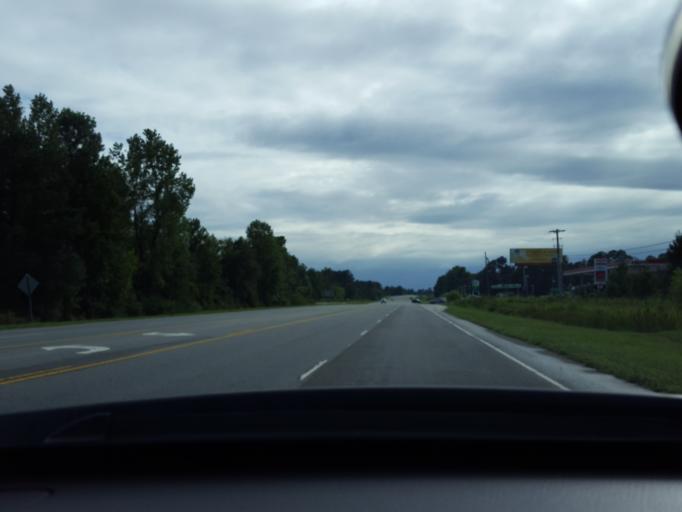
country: US
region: North Carolina
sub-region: Duplin County
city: Kenansville
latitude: 34.9228
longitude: -78.0183
